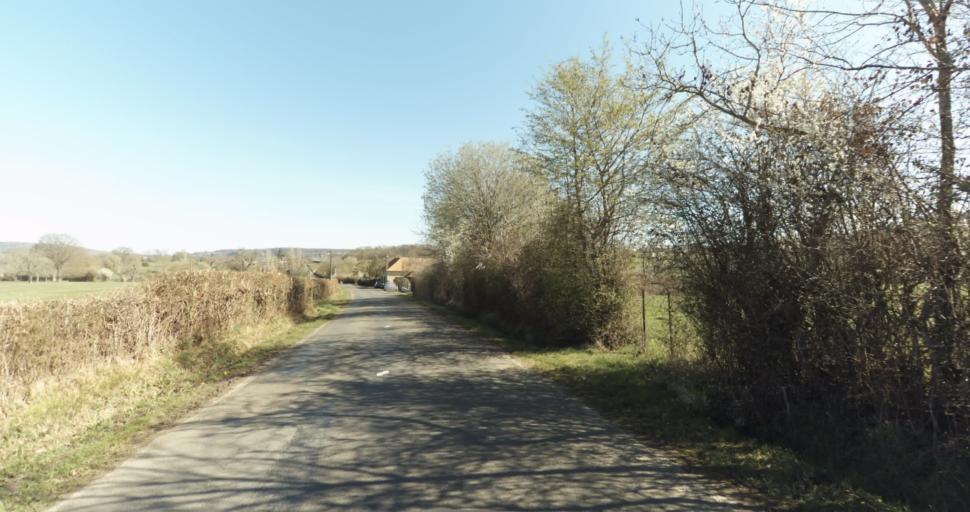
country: FR
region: Lower Normandy
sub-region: Departement de l'Orne
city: Trun
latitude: 48.9448
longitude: 0.0423
